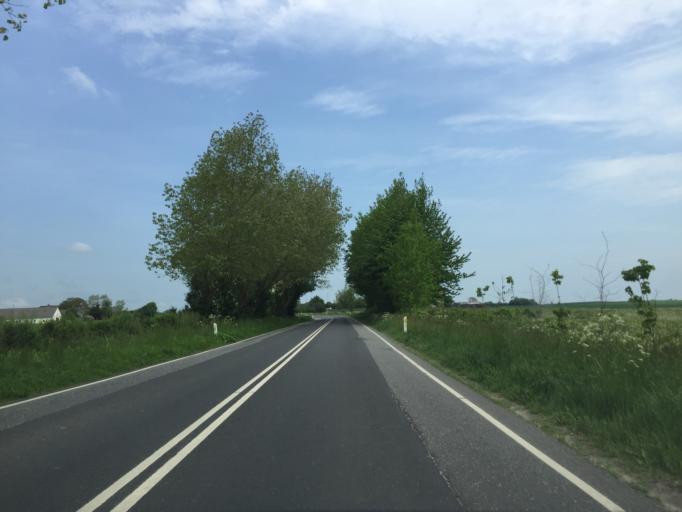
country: DK
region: South Denmark
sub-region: Svendborg Kommune
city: Thuro By
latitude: 55.1762
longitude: 10.7330
